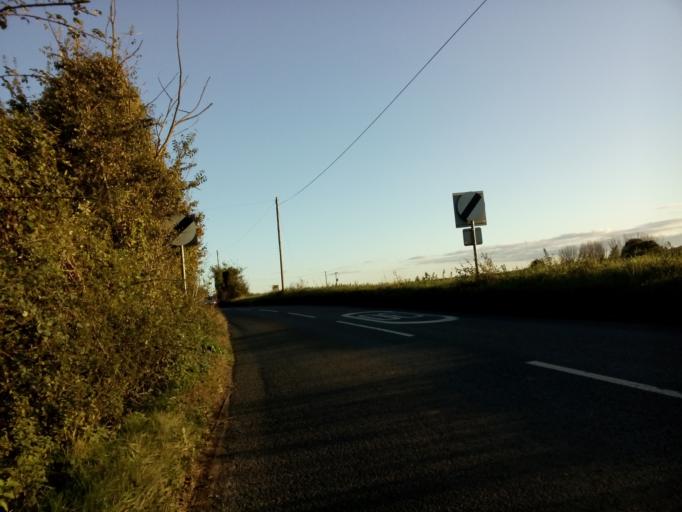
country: GB
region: England
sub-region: Suffolk
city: Sudbury
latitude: 52.0094
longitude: 0.7506
